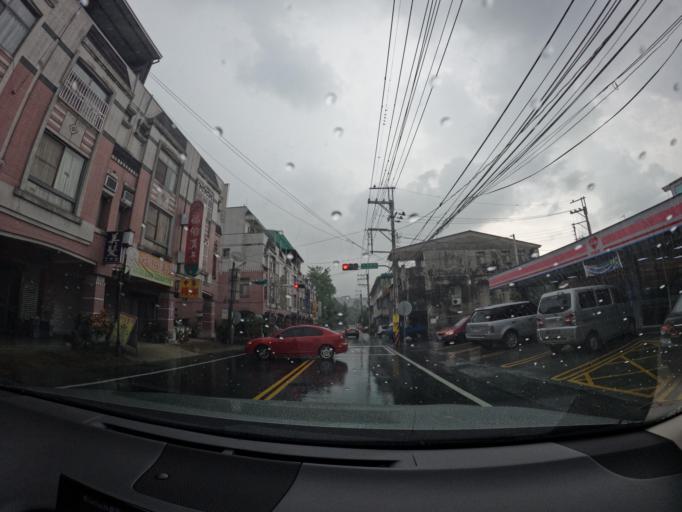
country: TW
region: Taiwan
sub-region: Nantou
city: Nantou
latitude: 23.8939
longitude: 120.7311
